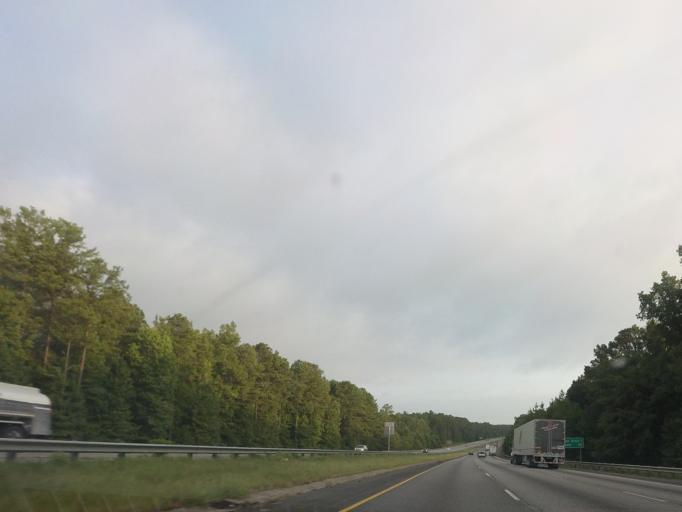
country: US
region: Georgia
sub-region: Henry County
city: Locust Grove
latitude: 33.2747
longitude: -84.1043
